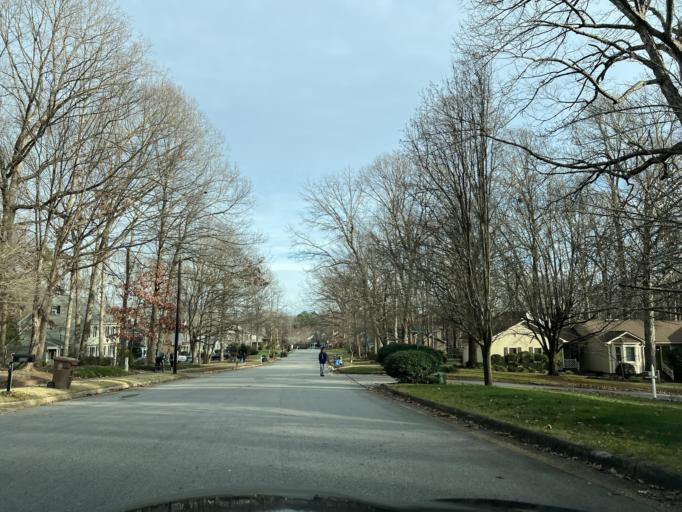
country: US
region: North Carolina
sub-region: Wake County
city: Cary
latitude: 35.8018
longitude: -78.7462
